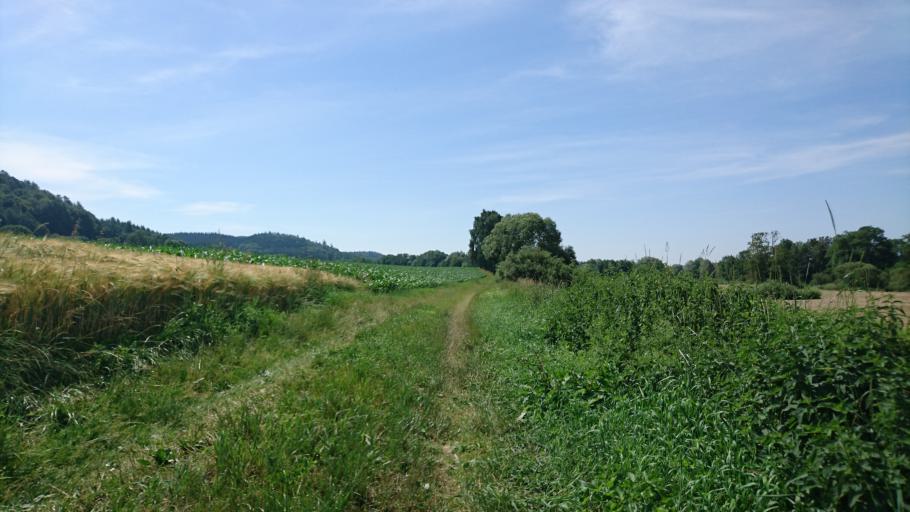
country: DE
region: Bavaria
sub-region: Swabia
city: Zusmarshausen
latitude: 48.4297
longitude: 10.5965
